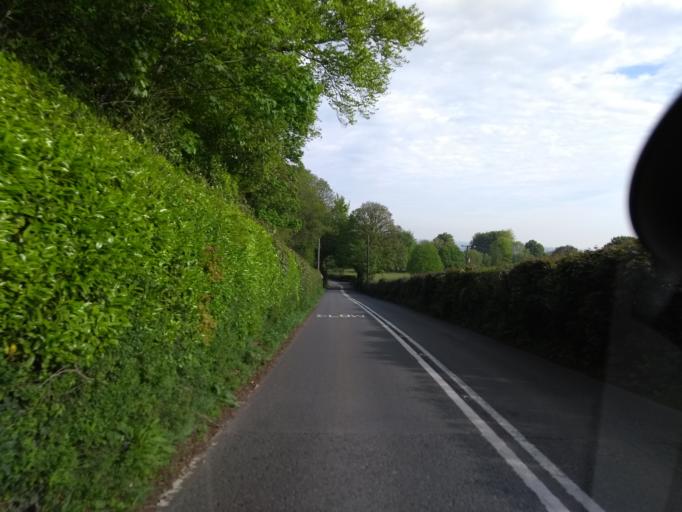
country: GB
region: England
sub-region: Devon
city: Axminster
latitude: 50.7706
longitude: -2.9795
